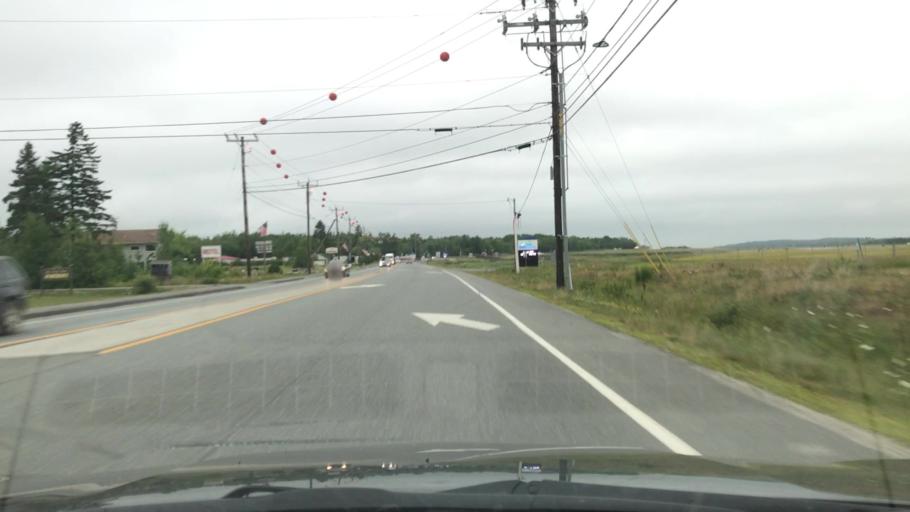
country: US
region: Maine
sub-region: Hancock County
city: Trenton
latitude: 44.4405
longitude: -68.3701
